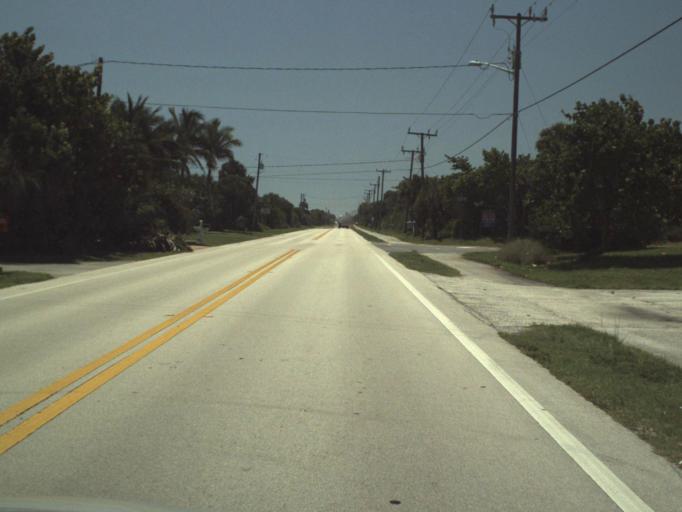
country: US
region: Florida
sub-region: Brevard County
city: Grant-Valkaria
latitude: 27.9612
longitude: -80.5053
